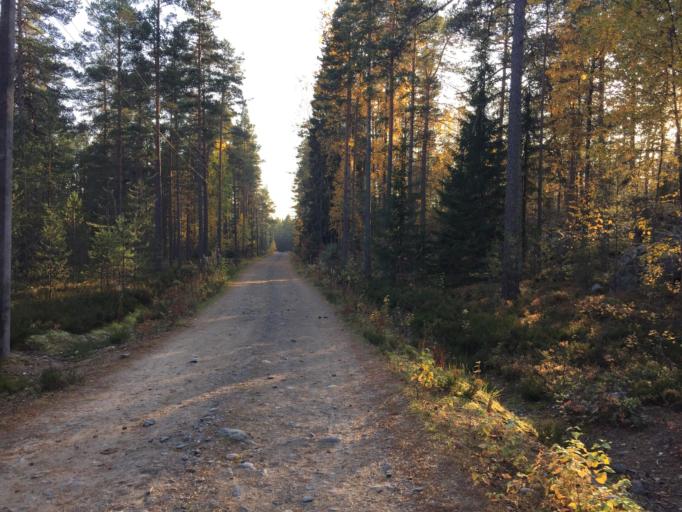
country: RU
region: Leningrad
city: Priozersk
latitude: 61.2832
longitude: 30.1036
